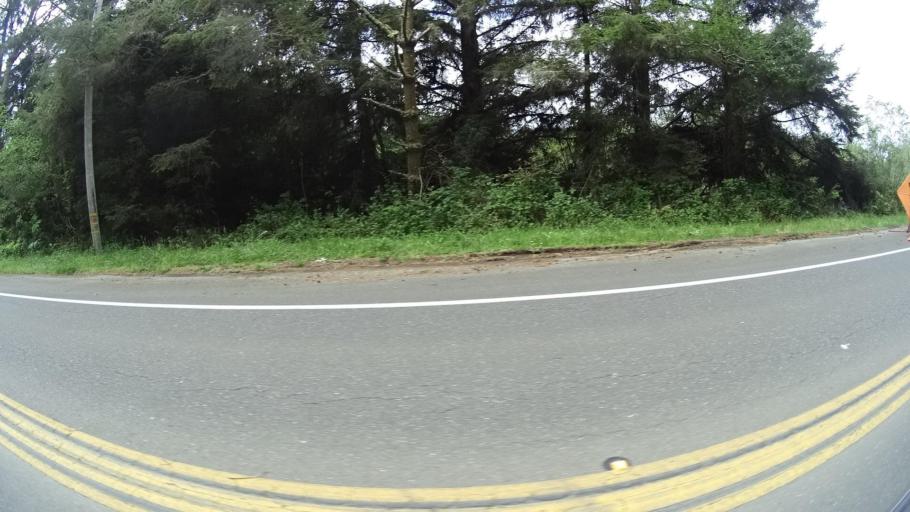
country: US
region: California
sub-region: Humboldt County
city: Humboldt Hill
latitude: 40.7016
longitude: -124.2048
